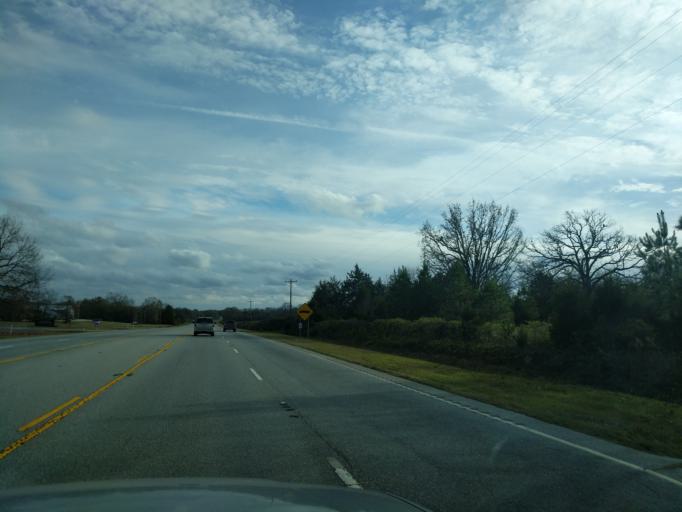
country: US
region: South Carolina
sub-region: Anderson County
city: Honea Path
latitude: 34.5212
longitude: -82.3125
